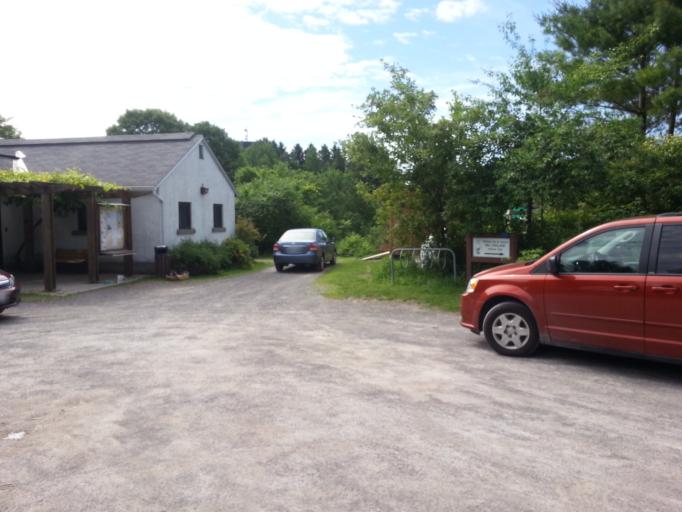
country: CA
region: Ontario
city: Ottawa
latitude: 45.3870
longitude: -75.7034
